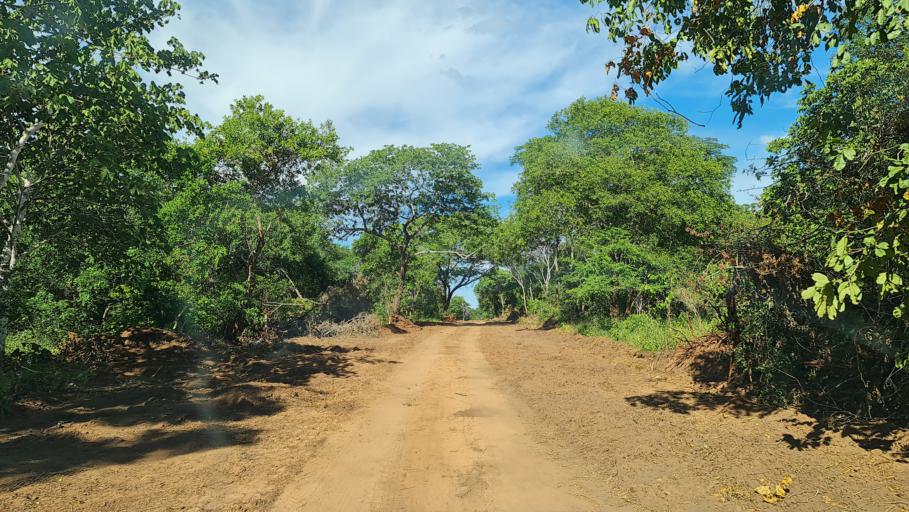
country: MZ
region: Nampula
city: Antonio Enes
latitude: -15.5092
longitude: 40.1364
